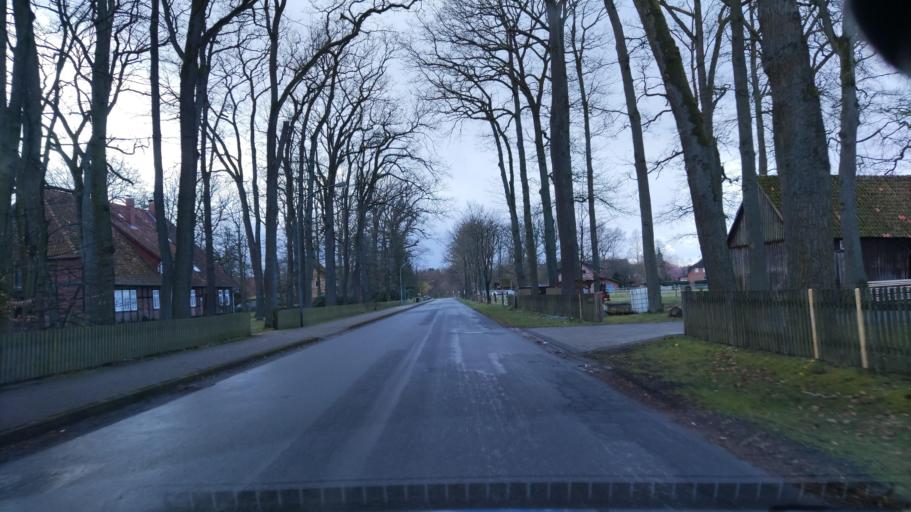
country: DE
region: Lower Saxony
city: Hermannsburg
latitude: 52.8364
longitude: 10.1403
